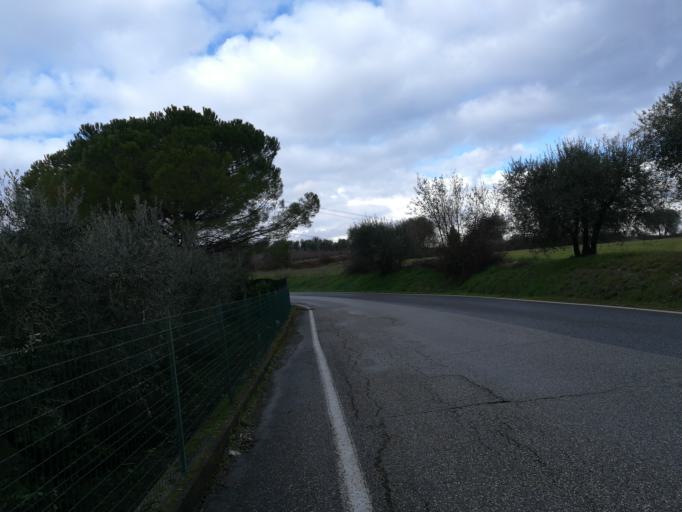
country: IT
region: Tuscany
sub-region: Provincia di Prato
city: Comeana
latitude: 43.7965
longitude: 11.0452
